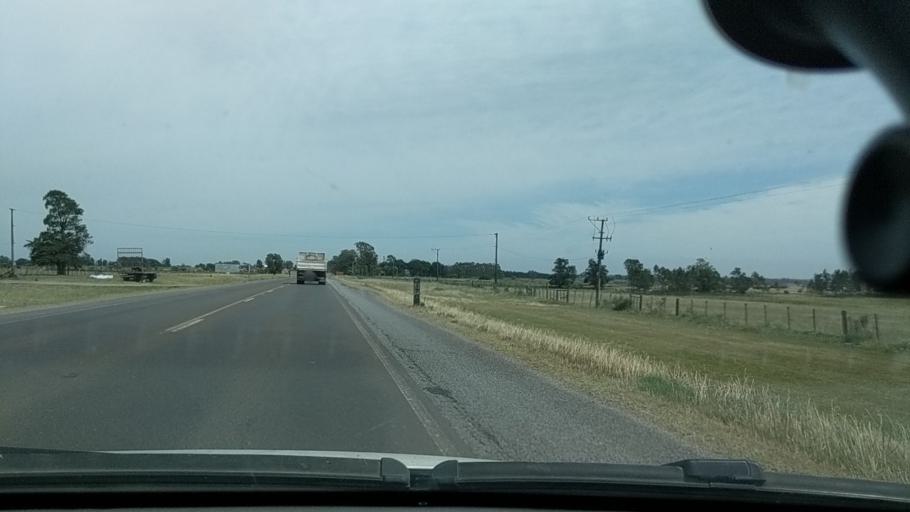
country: UY
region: Durazno
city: Durazno
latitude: -33.4313
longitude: -56.4944
